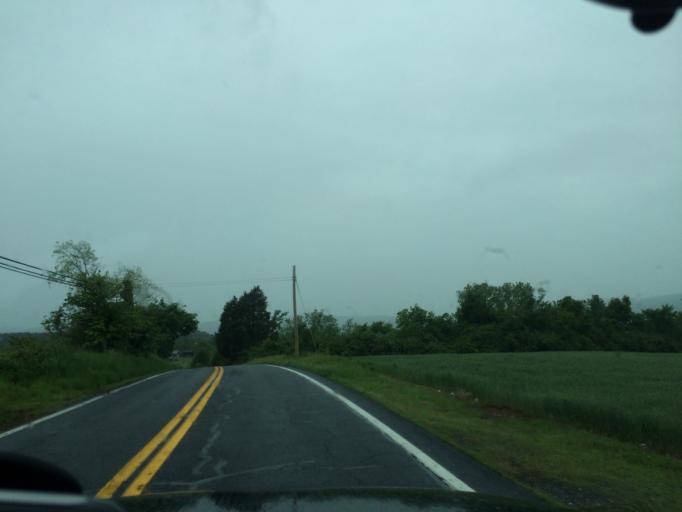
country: US
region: Maryland
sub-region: Frederick County
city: Thurmont
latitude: 39.6168
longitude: -77.3711
